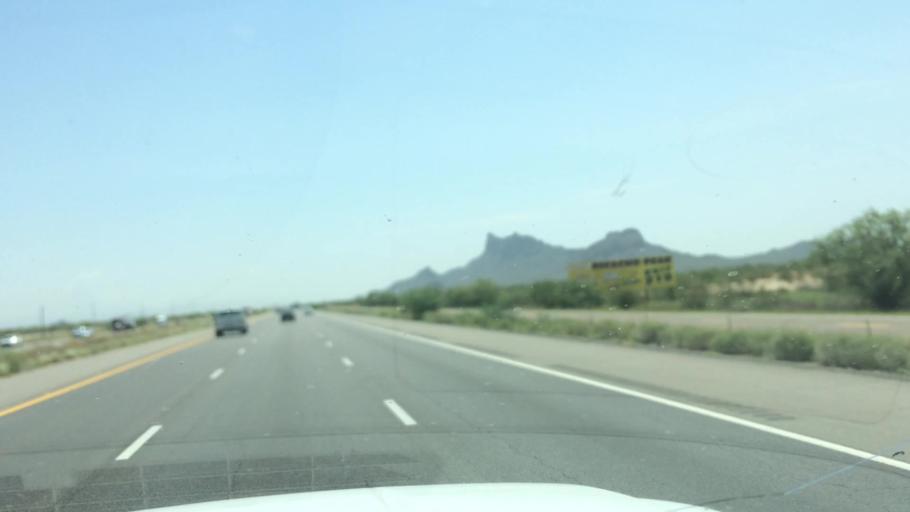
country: US
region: Arizona
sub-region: Pinal County
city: Eloy
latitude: 32.6853
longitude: -111.4509
